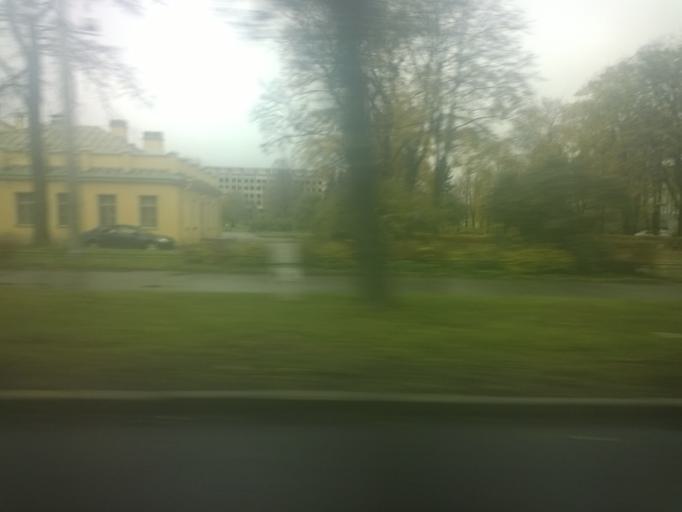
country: RU
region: St.-Petersburg
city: Avtovo
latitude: 59.8858
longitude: 30.2668
